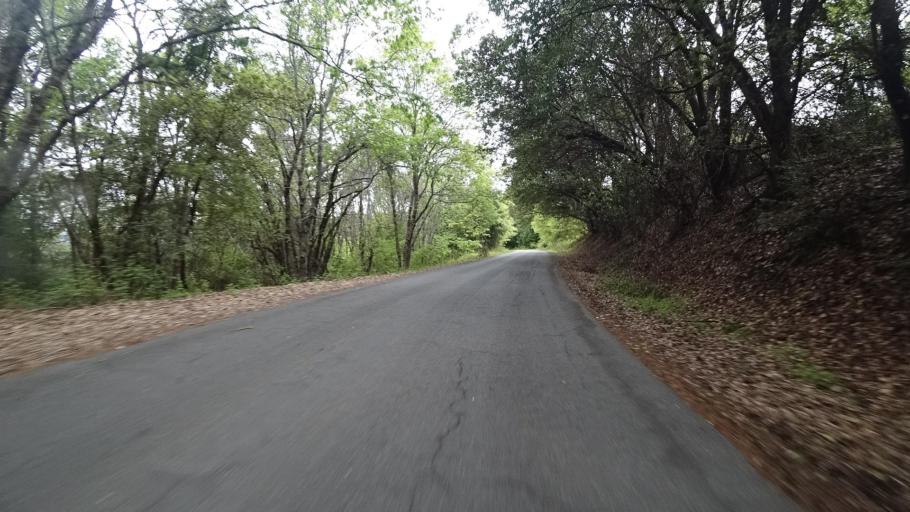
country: US
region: California
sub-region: Humboldt County
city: Willow Creek
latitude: 41.1156
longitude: -123.7193
